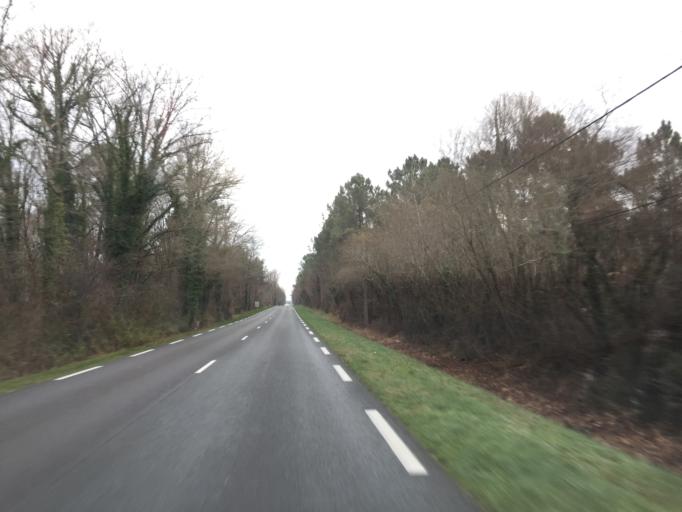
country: FR
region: Aquitaine
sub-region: Departement de la Gironde
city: Saint-Sauveur
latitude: 45.1865
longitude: -0.8481
